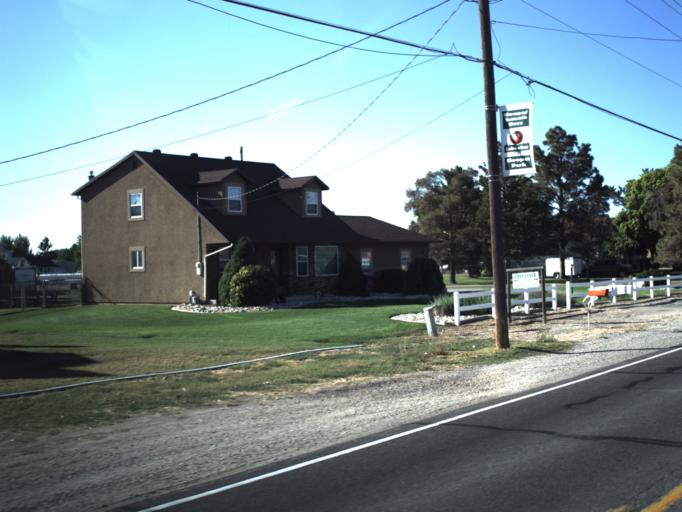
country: US
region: Utah
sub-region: Weber County
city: Hooper
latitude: 41.1578
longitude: -112.1229
